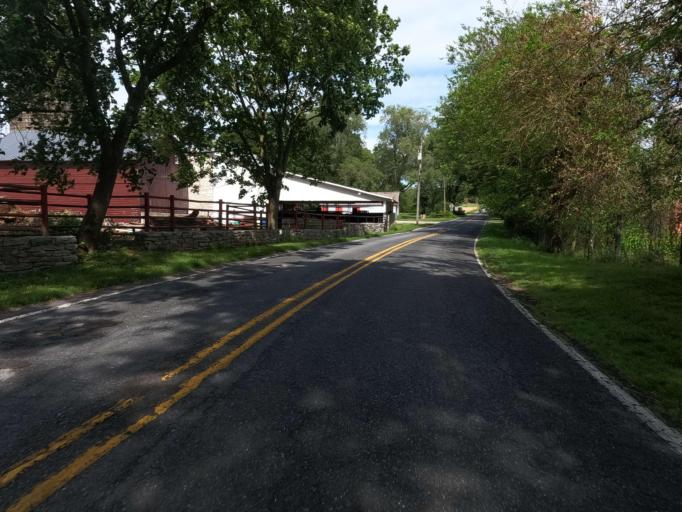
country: US
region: Pennsylvania
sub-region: Lebanon County
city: Campbelltown
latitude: 40.2705
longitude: -76.6033
